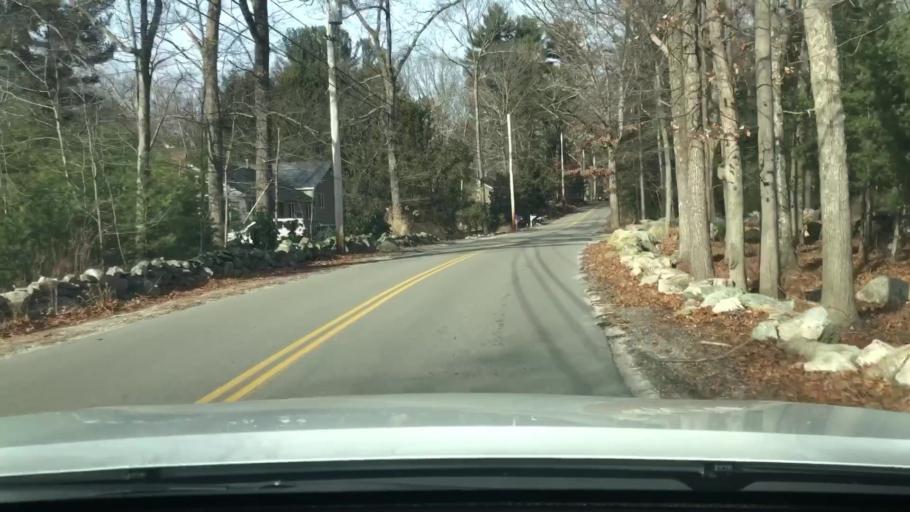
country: US
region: Massachusetts
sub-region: Norfolk County
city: Bellingham
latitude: 42.1063
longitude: -71.4958
